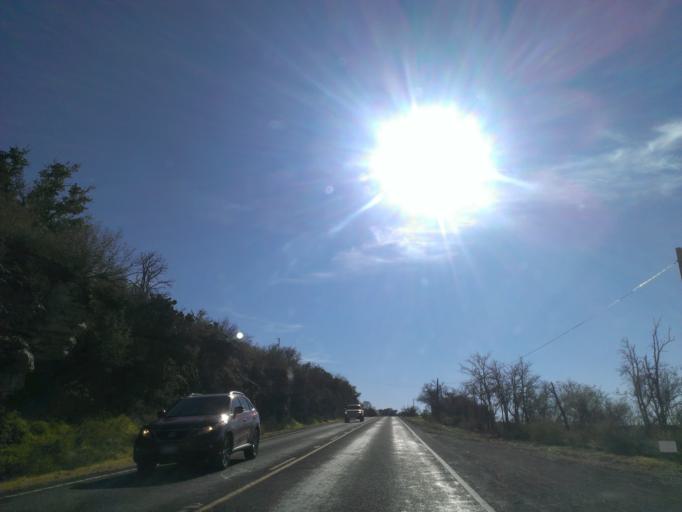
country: US
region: Texas
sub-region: Burnet County
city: Meadowlakes
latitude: 30.5557
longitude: -98.2845
